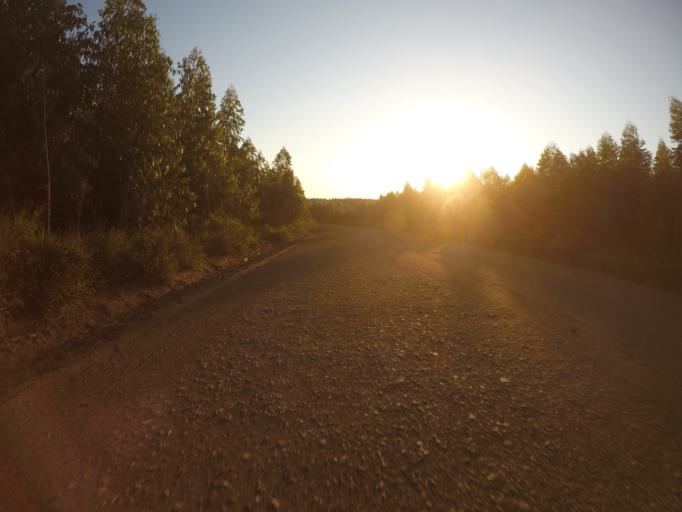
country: ZA
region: KwaZulu-Natal
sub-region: uThungulu District Municipality
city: KwaMbonambi
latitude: -28.6649
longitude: 32.0597
